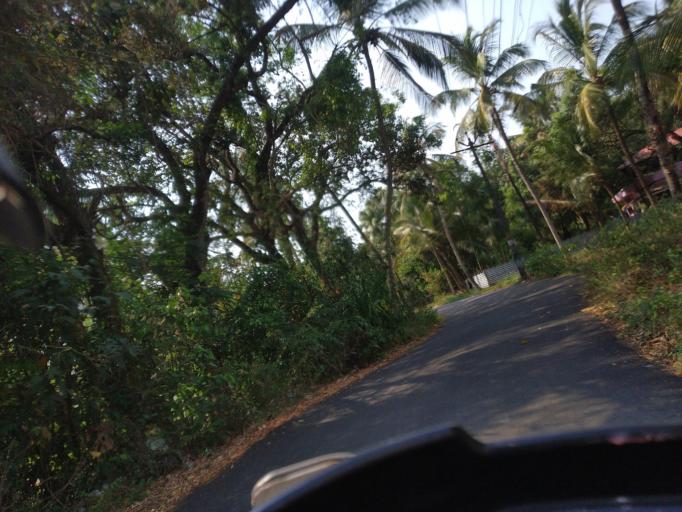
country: IN
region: Kerala
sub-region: Thrissur District
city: Thanniyam
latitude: 10.4383
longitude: 76.0807
